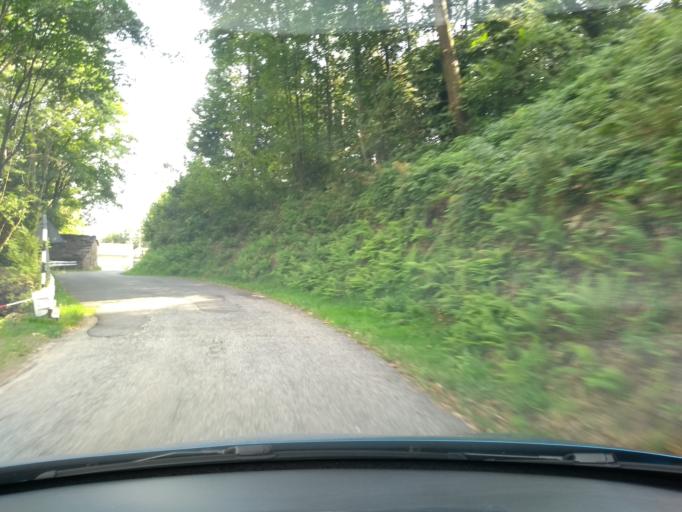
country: IT
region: Piedmont
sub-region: Provincia di Torino
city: Corio
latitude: 45.3270
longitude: 7.5172
